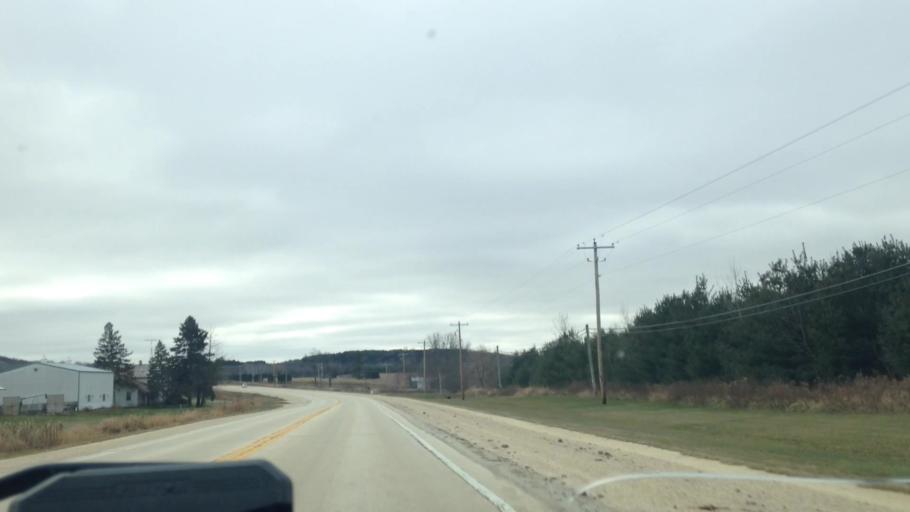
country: US
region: Wisconsin
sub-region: Dodge County
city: Mayville
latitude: 43.4680
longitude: -88.5465
